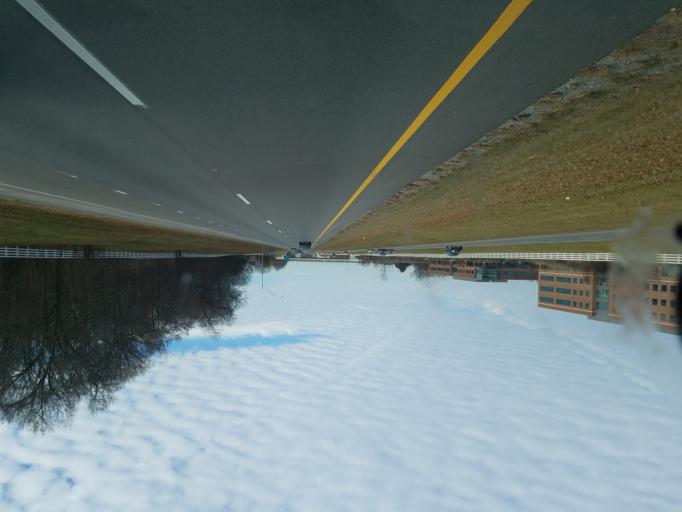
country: US
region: Ohio
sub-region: Franklin County
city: New Albany
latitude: 40.0910
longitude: -82.8167
